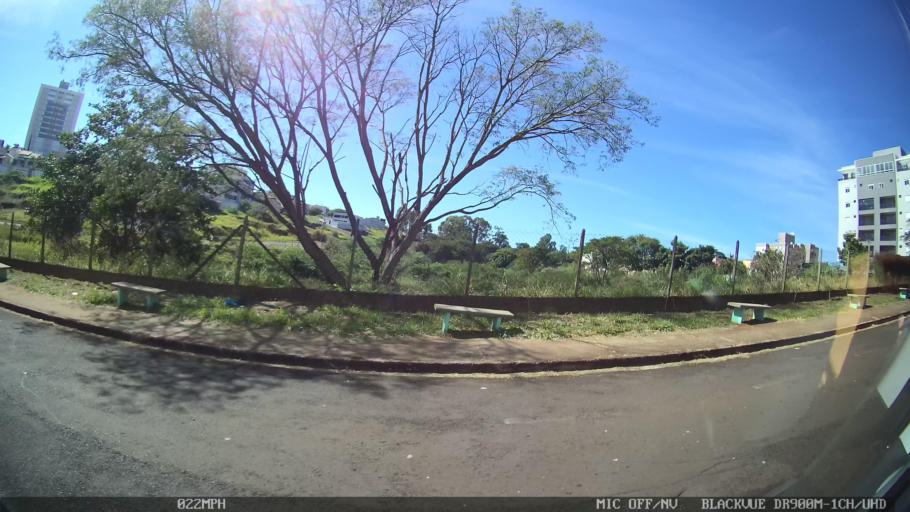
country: BR
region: Sao Paulo
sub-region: Franca
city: Franca
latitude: -20.5529
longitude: -47.4006
